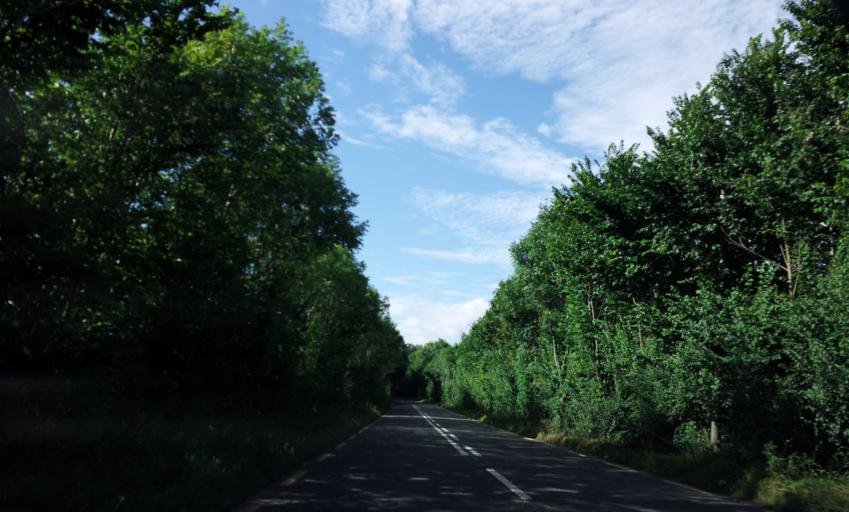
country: IE
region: Munster
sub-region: County Cork
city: Macroom
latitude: 51.9140
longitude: -9.0535
